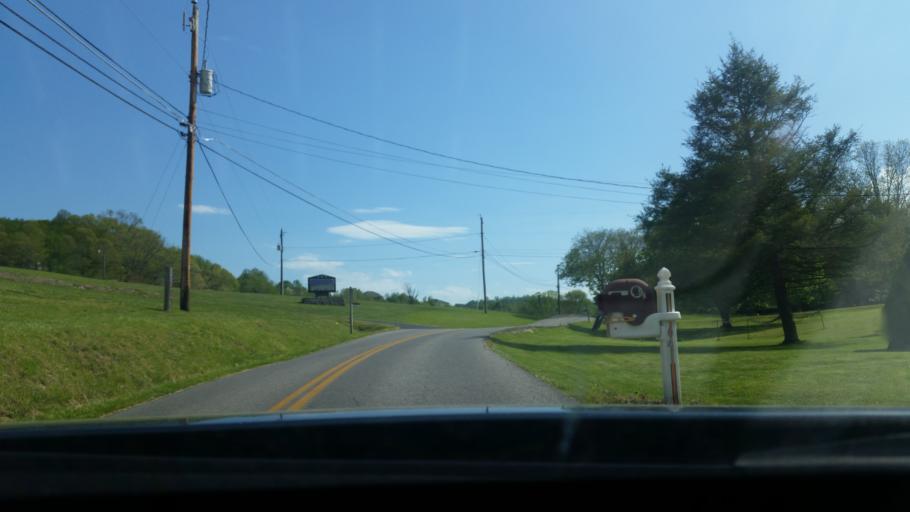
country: US
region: Virginia
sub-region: Giles County
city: Pembroke
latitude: 37.3122
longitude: -80.6320
